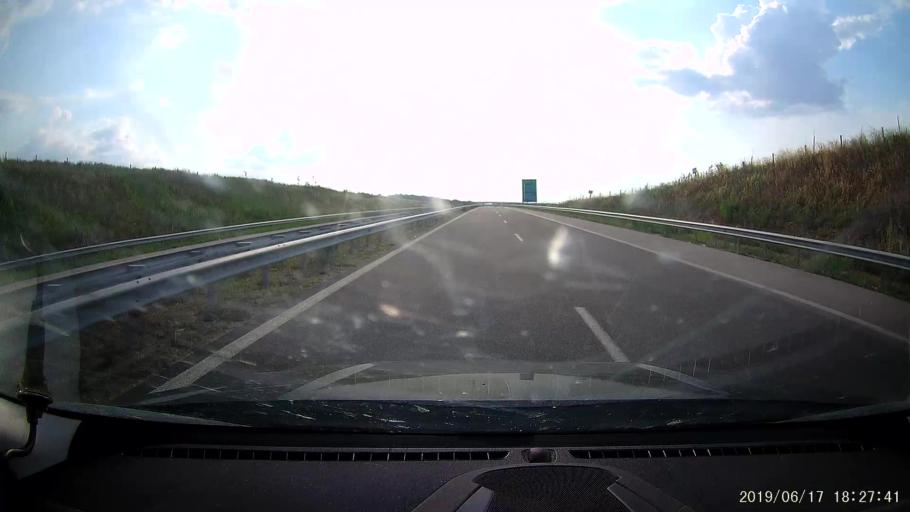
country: BG
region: Khaskovo
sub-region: Obshtina Dimitrovgrad
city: Dimitrovgrad
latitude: 42.0182
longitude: 25.6021
